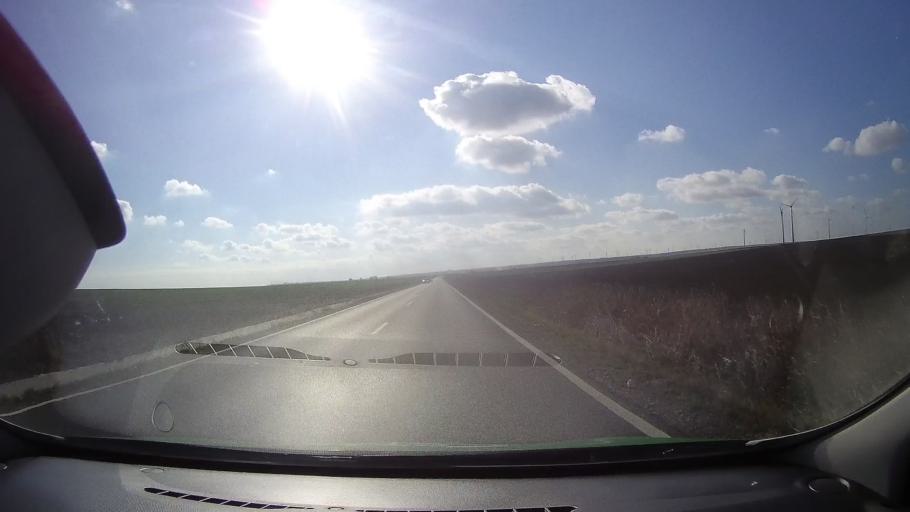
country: RO
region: Constanta
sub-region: Comuna Mihai Viteazu
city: Mihai Viteazu
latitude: 44.6725
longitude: 28.6843
